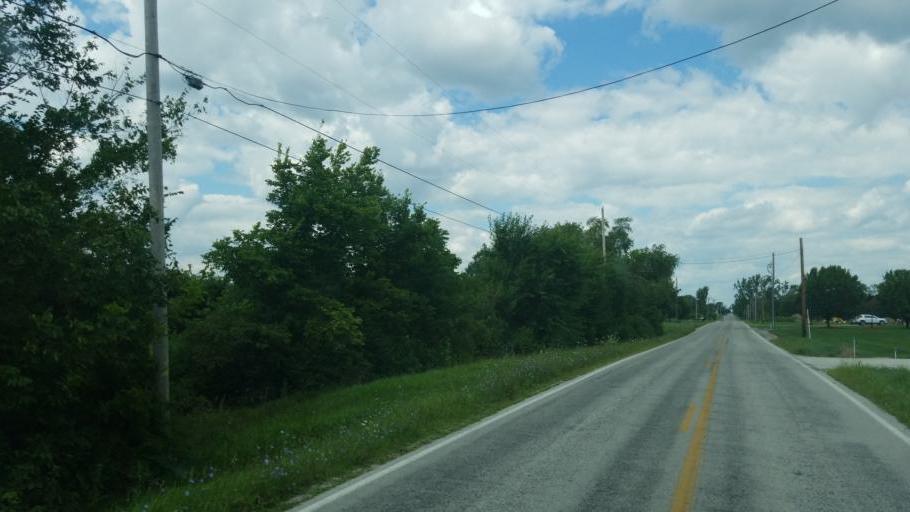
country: US
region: Ohio
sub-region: Ottawa County
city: Elmore
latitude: 41.5353
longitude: -83.2801
